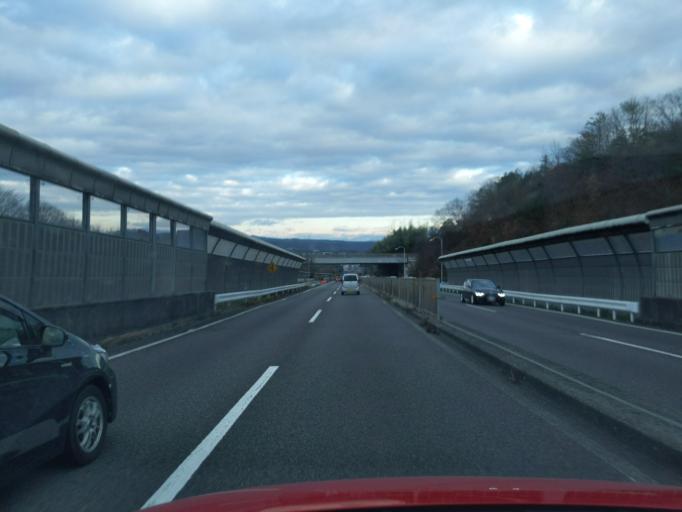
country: JP
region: Gifu
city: Toki
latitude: 35.3455
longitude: 137.1624
